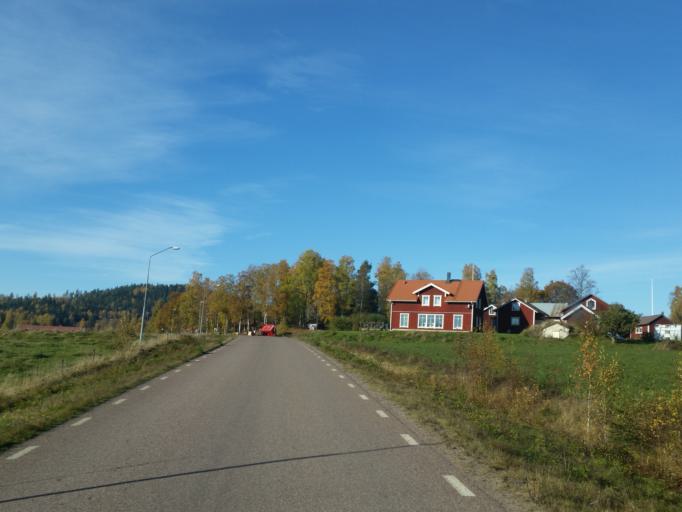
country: SE
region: Dalarna
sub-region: Borlange Kommun
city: Ornas
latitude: 60.4466
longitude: 15.6353
